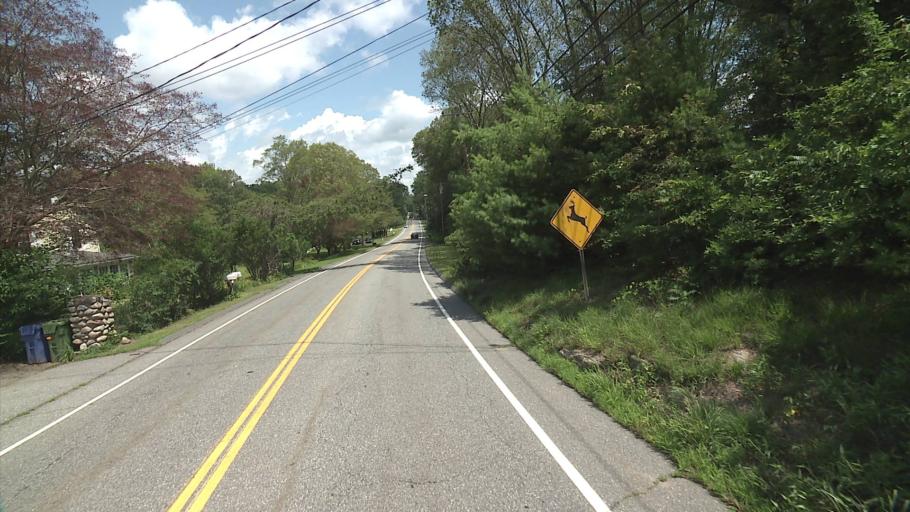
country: US
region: Connecticut
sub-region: Middlesex County
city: Chester Center
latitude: 41.4055
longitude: -72.4418
